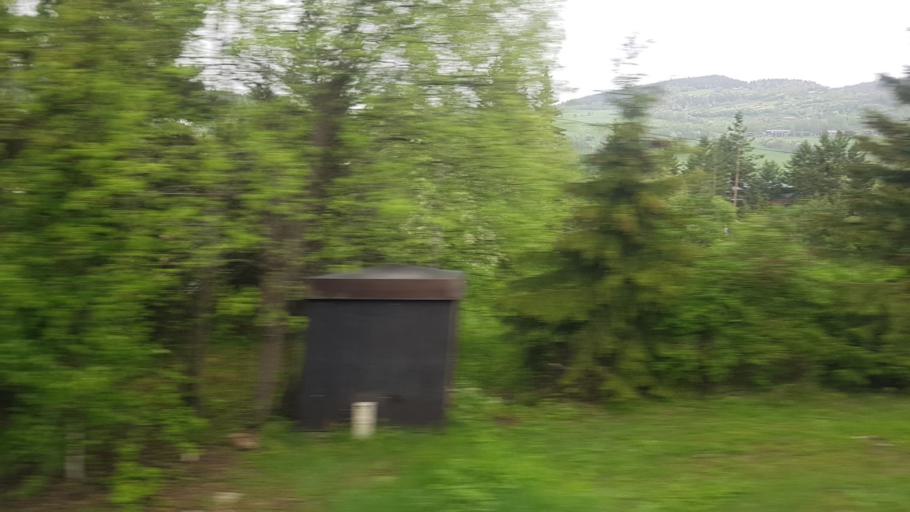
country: NO
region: Oppland
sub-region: Nord-Fron
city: Vinstra
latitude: 61.5831
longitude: 9.7600
